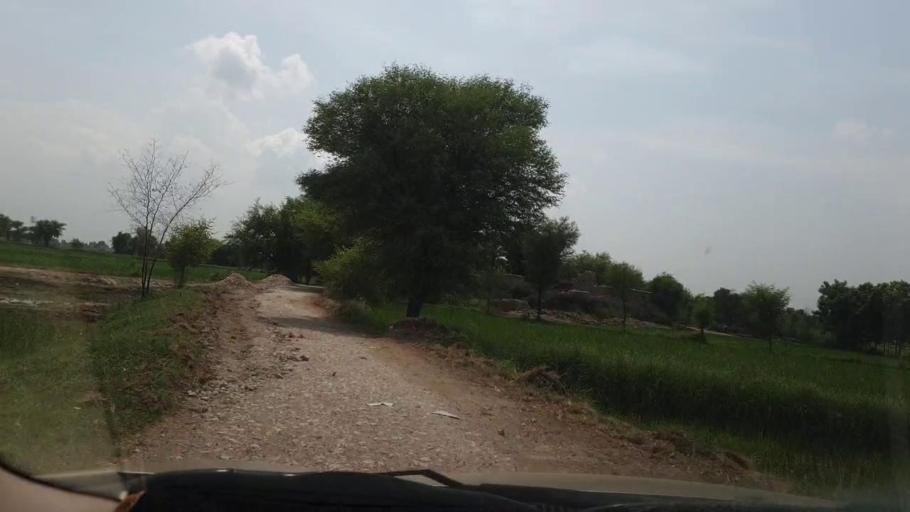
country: PK
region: Sindh
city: Larkana
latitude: 27.5720
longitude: 68.1106
